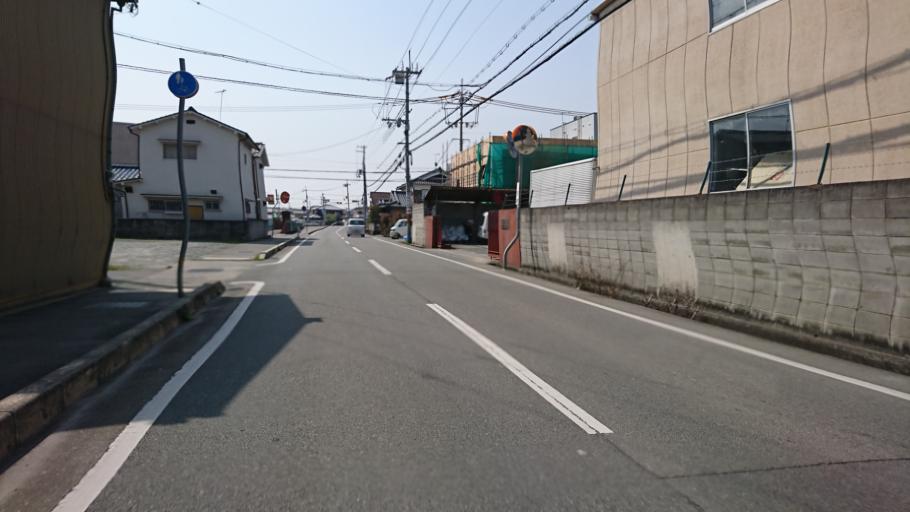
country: JP
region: Hyogo
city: Shirahamacho-usazakiminami
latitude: 34.7865
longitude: 134.7510
